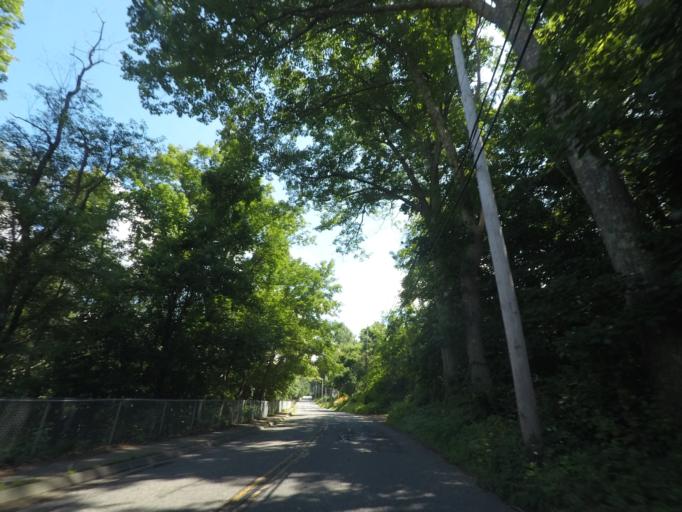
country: US
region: Massachusetts
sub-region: Hampden County
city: Palmer
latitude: 42.1535
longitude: -72.3324
